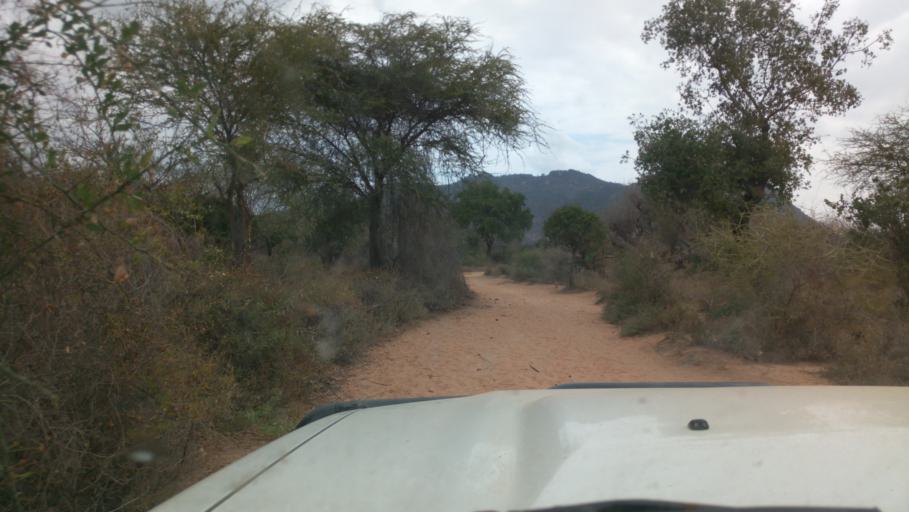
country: KE
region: Kitui
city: Kitui
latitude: -1.8175
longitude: 38.4250
